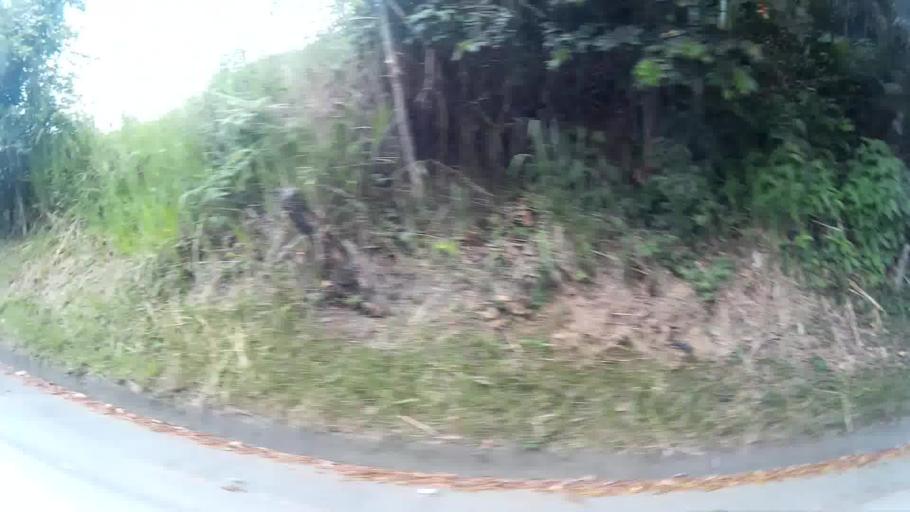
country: CO
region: Risaralda
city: La Virginia
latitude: 4.8783
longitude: -75.8707
